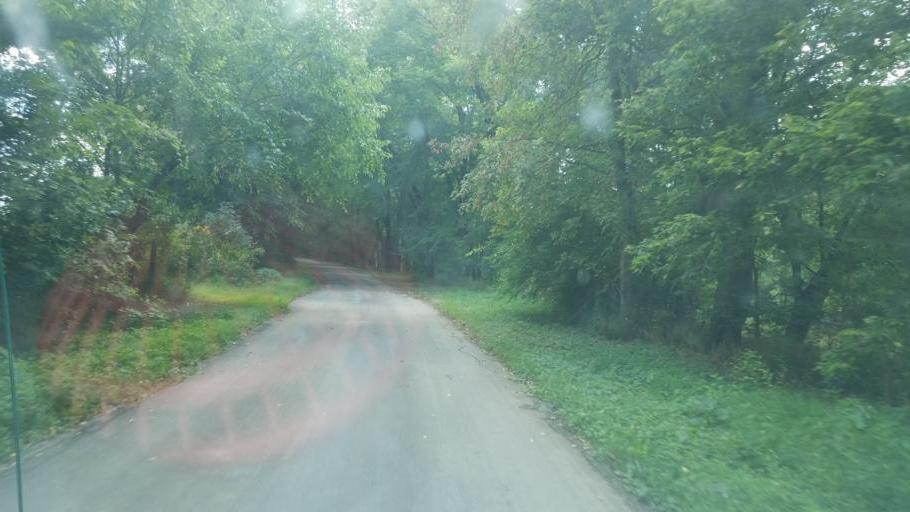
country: US
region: Ohio
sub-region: Marion County
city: Prospect
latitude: 40.4344
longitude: -83.1937
